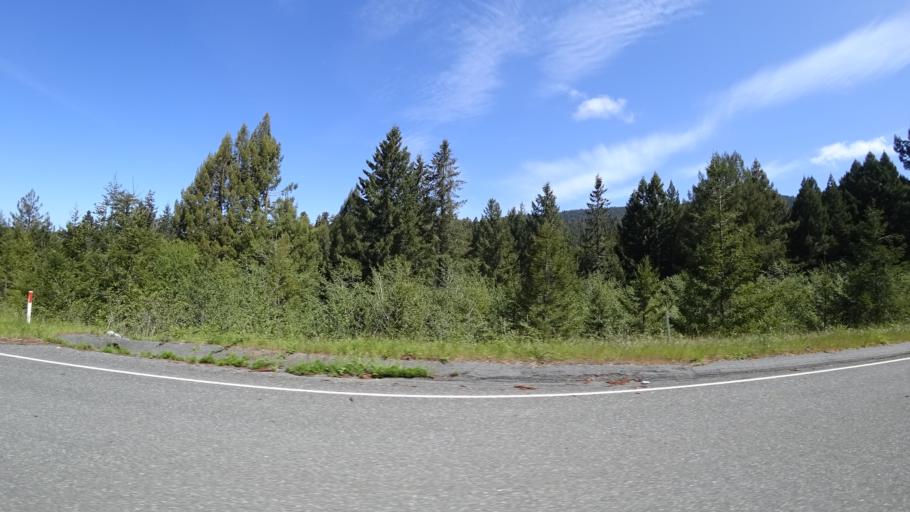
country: US
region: California
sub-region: Humboldt County
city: Westhaven-Moonstone
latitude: 41.3594
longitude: -123.9998
